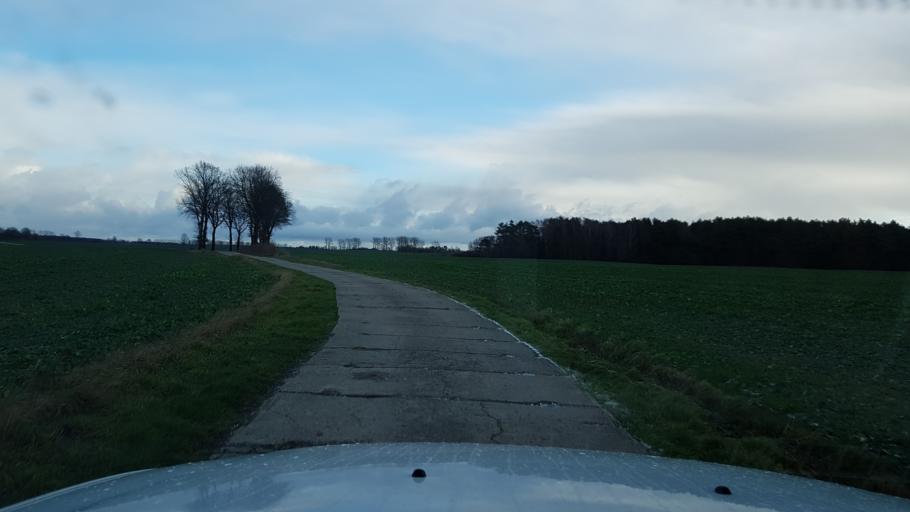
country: PL
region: West Pomeranian Voivodeship
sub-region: Powiat gryficki
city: Brojce
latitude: 54.0354
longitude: 15.3802
